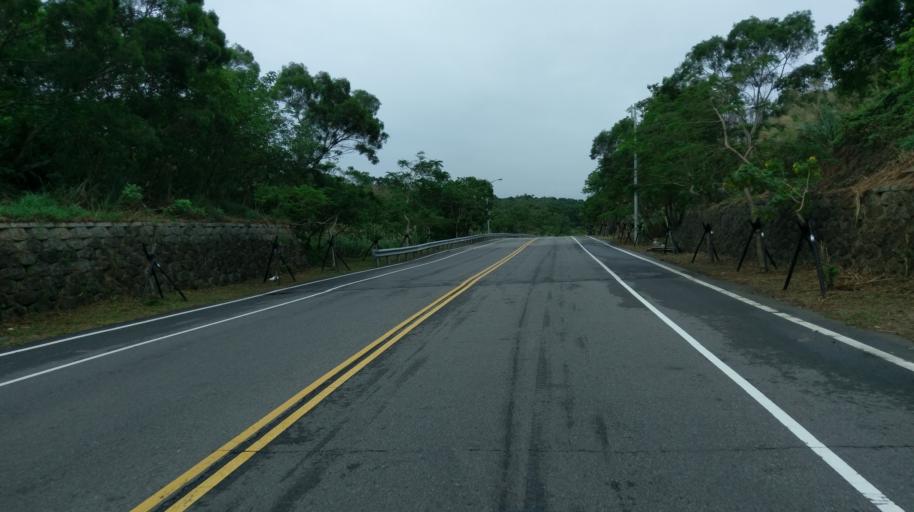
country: TW
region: Taiwan
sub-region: Miaoli
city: Miaoli
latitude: 24.6253
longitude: 120.8271
